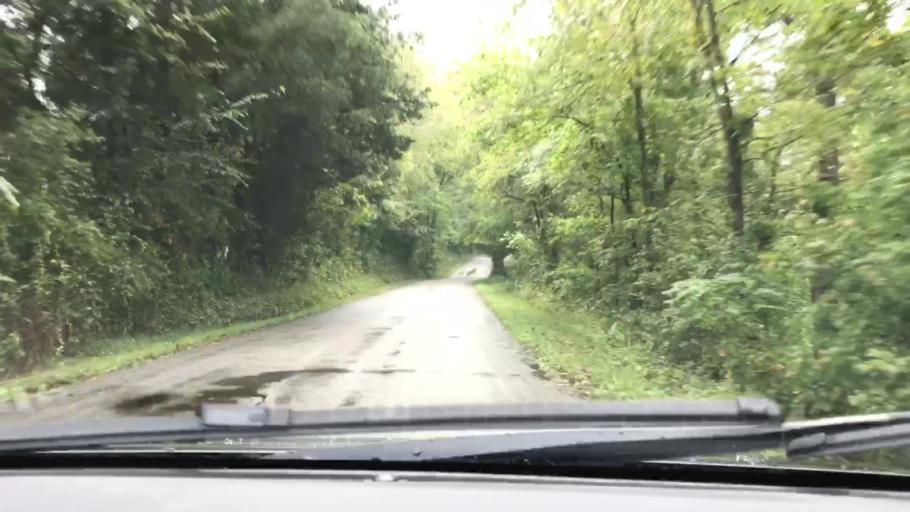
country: US
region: Tennessee
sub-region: Macon County
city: Red Boiling Springs
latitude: 36.5864
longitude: -85.7772
